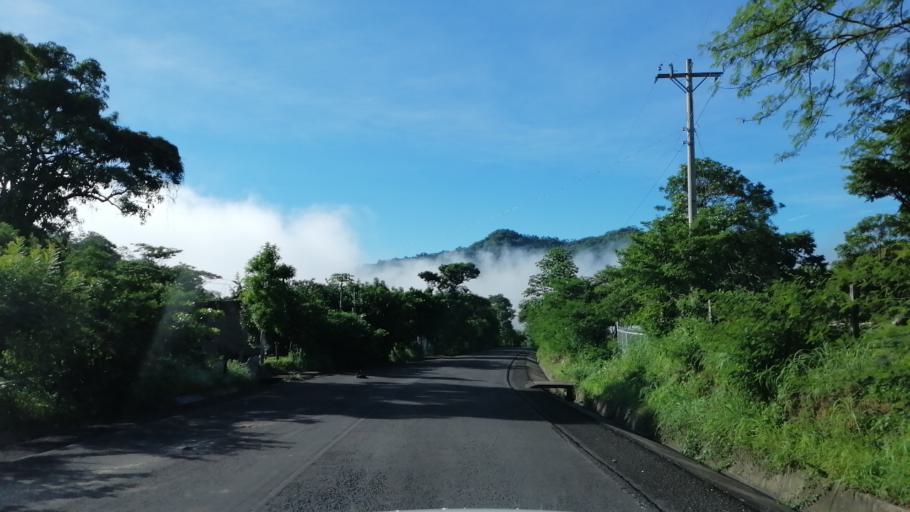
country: SV
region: Morazan
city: Cacaopera
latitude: 13.7772
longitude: -88.0970
